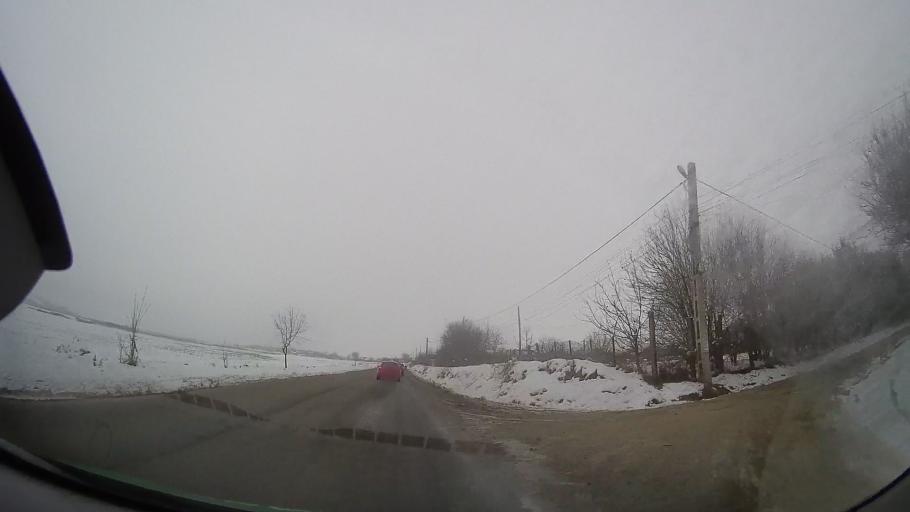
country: RO
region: Vaslui
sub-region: Comuna Negresti
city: Negresti
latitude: 46.8377
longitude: 27.4398
